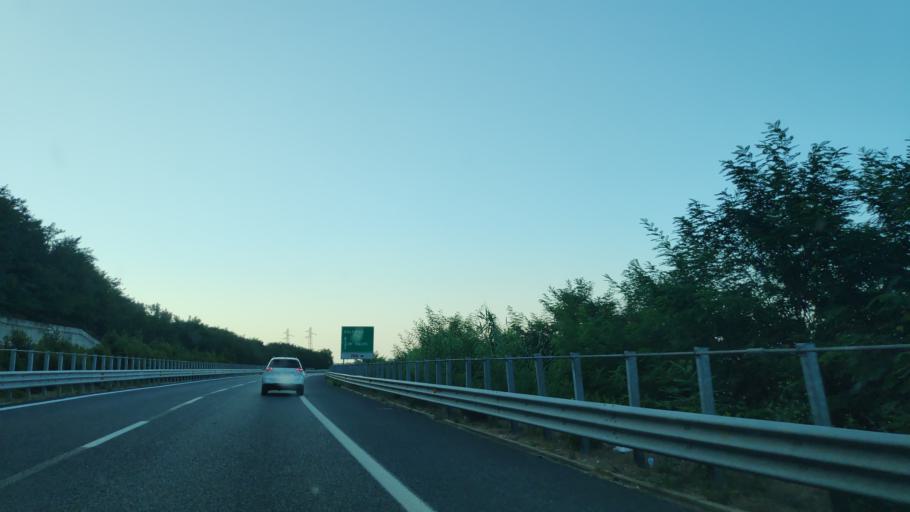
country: IT
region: Calabria
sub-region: Provincia di Reggio Calabria
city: Seminara
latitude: 38.3584
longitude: 15.8656
